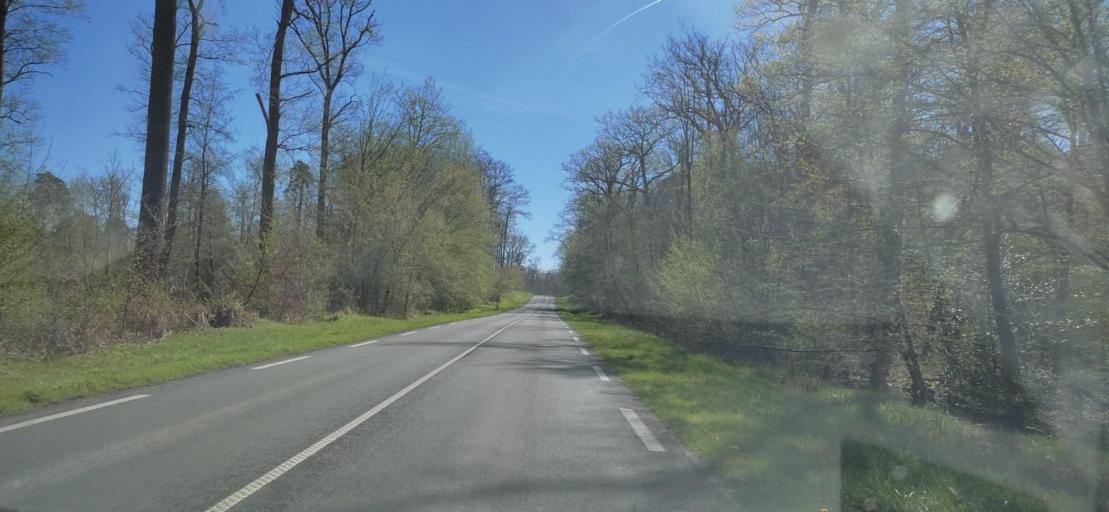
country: FR
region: Picardie
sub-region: Departement de l'Oise
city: Pierrefonds
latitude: 49.3669
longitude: 2.9435
